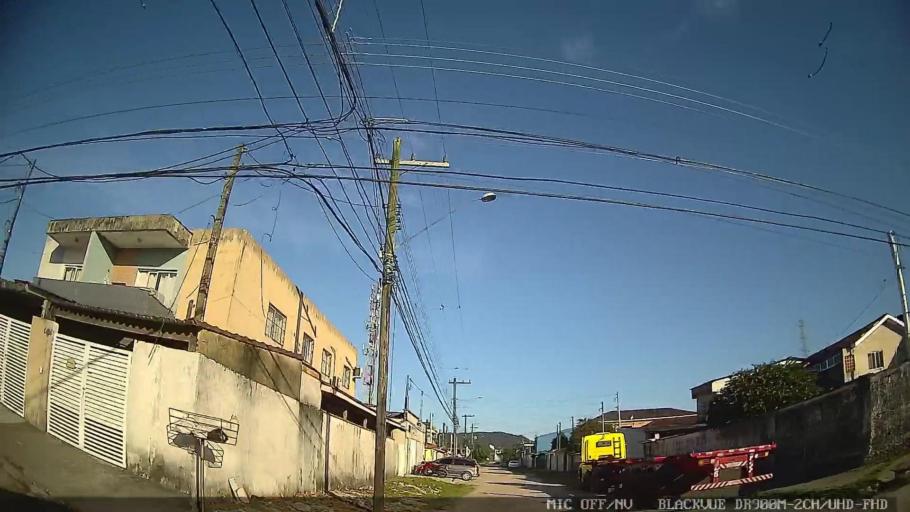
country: BR
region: Sao Paulo
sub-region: Guaruja
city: Guaruja
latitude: -23.9698
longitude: -46.2736
